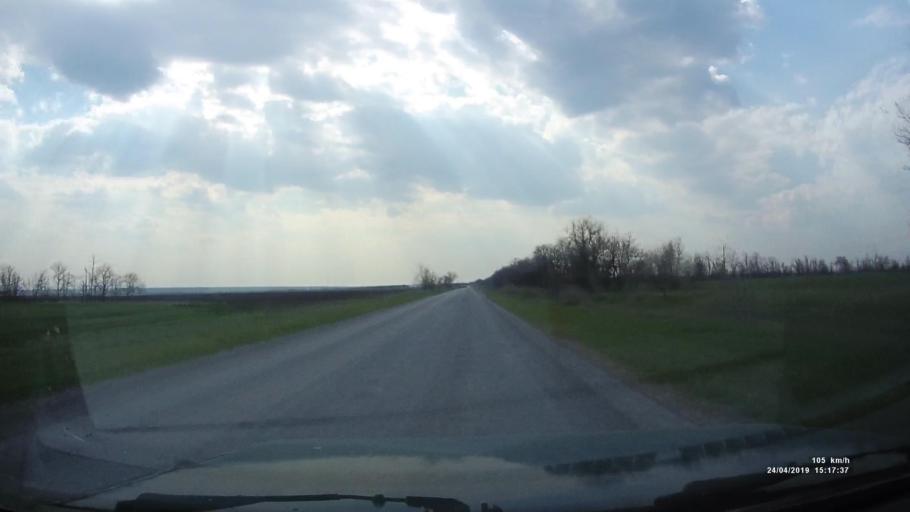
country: RU
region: Rostov
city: Remontnoye
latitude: 46.5465
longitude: 43.1854
